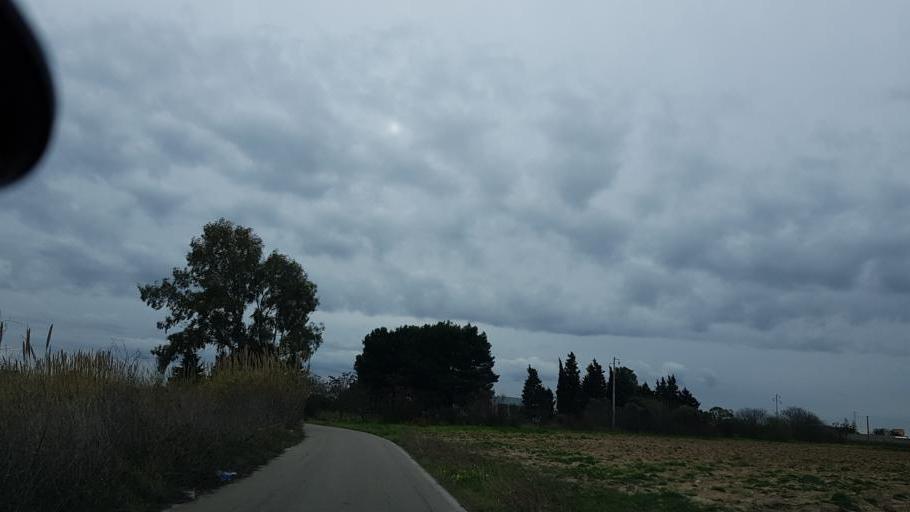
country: IT
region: Apulia
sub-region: Provincia di Brindisi
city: La Rosa
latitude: 40.6122
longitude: 17.9503
